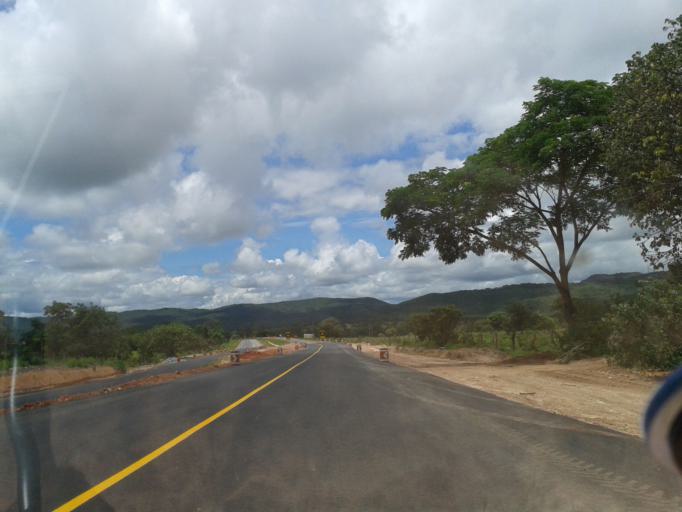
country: BR
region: Goias
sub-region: Goias
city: Goias
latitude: -15.9945
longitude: -50.0744
